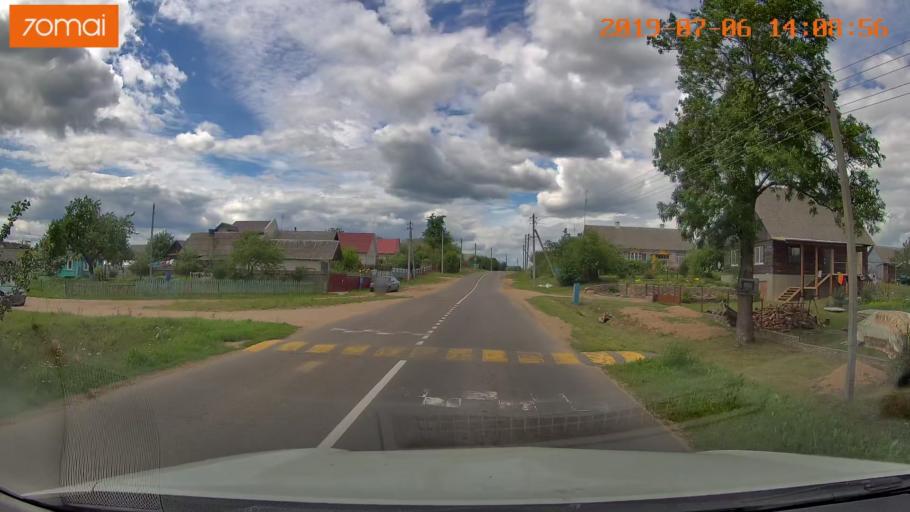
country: BY
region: Minsk
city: Ivyanyets
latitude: 53.8785
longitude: 26.7522
